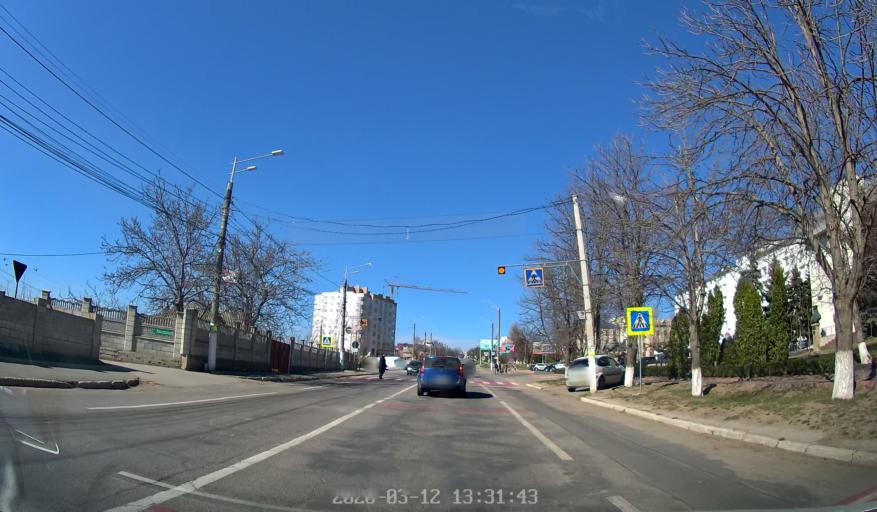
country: MD
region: Laloveni
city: Ialoveni
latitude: 46.9484
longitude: 28.7737
